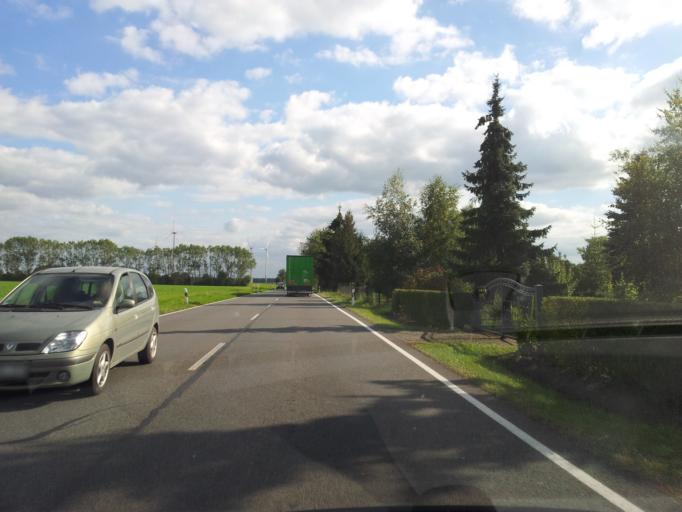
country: DE
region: Brandenburg
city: Sallgast
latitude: 51.6096
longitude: 13.8613
